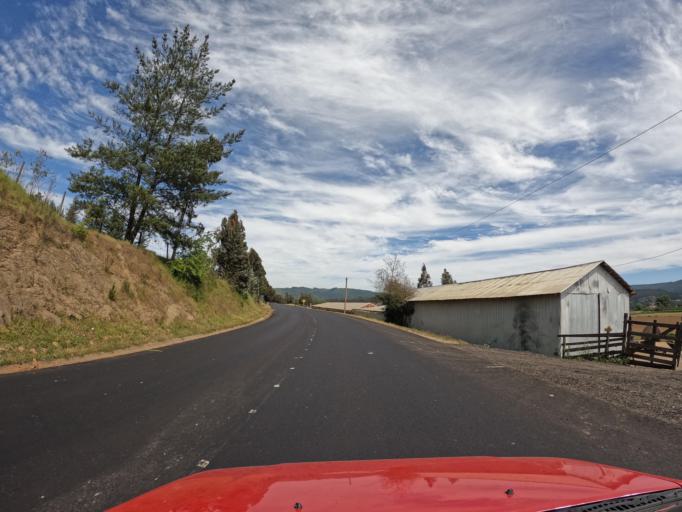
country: CL
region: Maule
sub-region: Provincia de Talca
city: Constitucion
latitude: -35.0758
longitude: -72.0391
